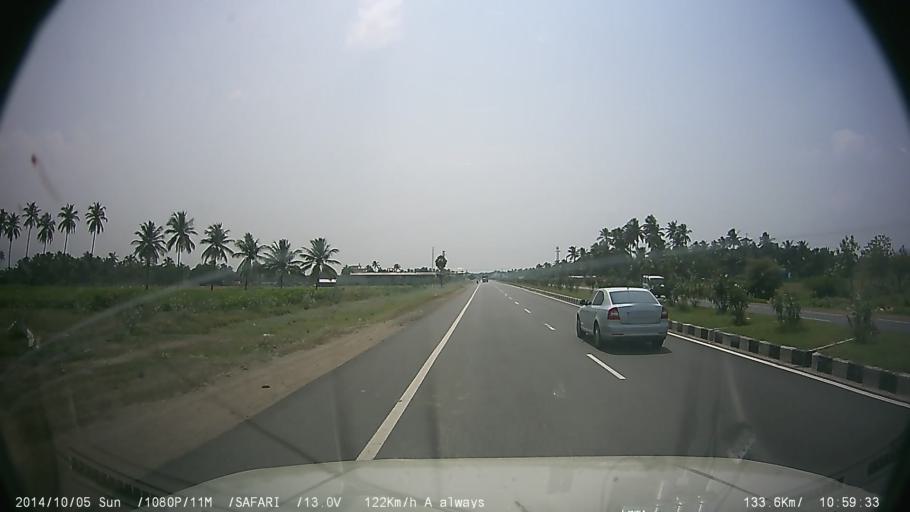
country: IN
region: Tamil Nadu
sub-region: Salem
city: Attur
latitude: 11.6336
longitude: 78.5326
